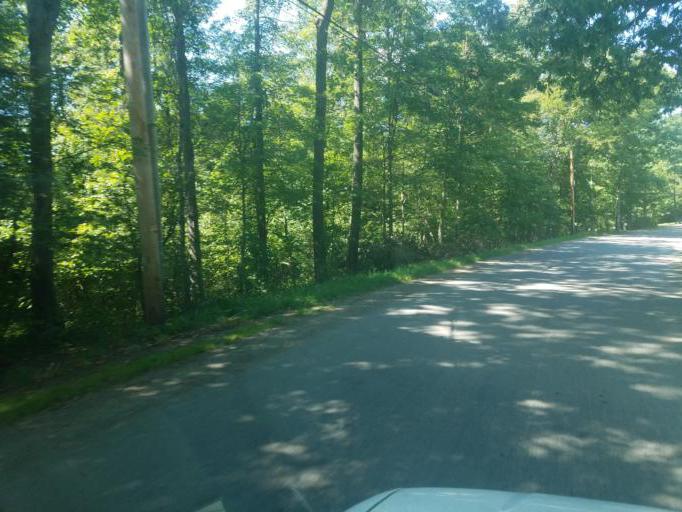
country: US
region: Pennsylvania
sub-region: Clarion County
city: Clarion
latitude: 41.1726
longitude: -79.4240
